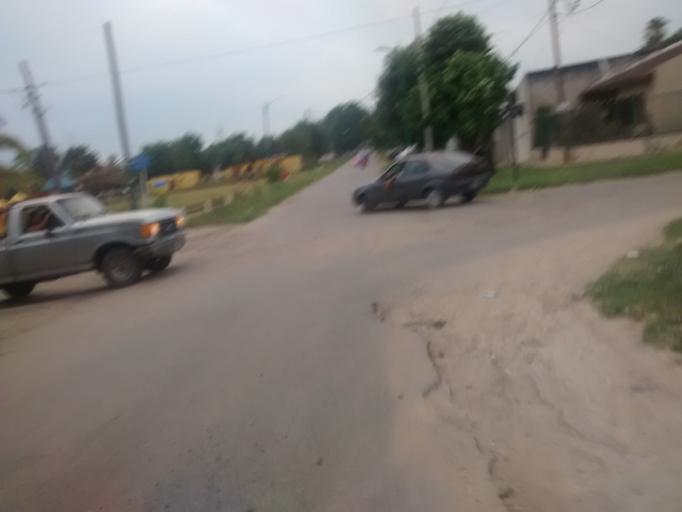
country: AR
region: Buenos Aires
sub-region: Partido de La Plata
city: La Plata
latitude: -34.9446
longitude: -57.9258
